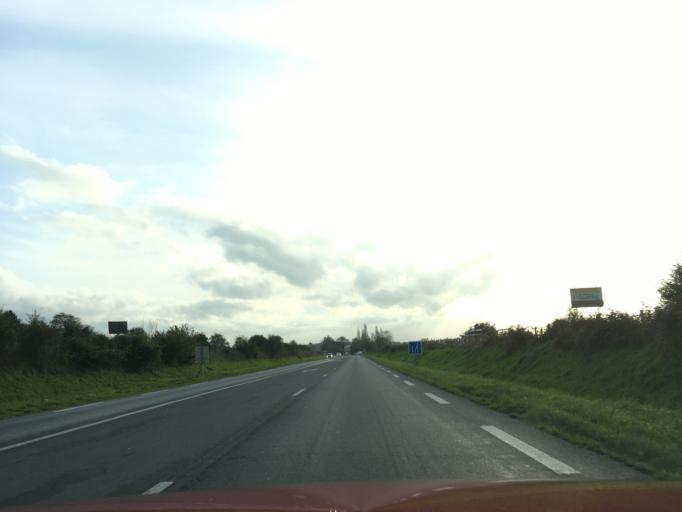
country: FR
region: Lower Normandy
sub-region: Departement de la Manche
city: Saint-Planchers
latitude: 48.8309
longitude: -1.5401
